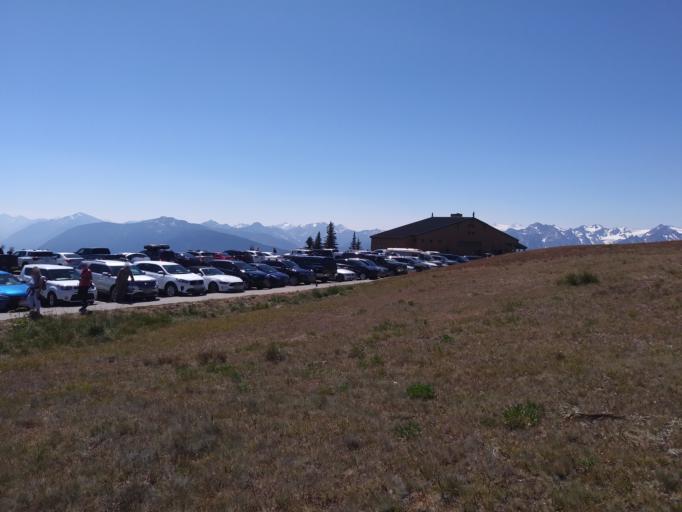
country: US
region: Washington
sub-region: Clallam County
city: Port Angeles
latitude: 47.9701
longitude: -123.4976
